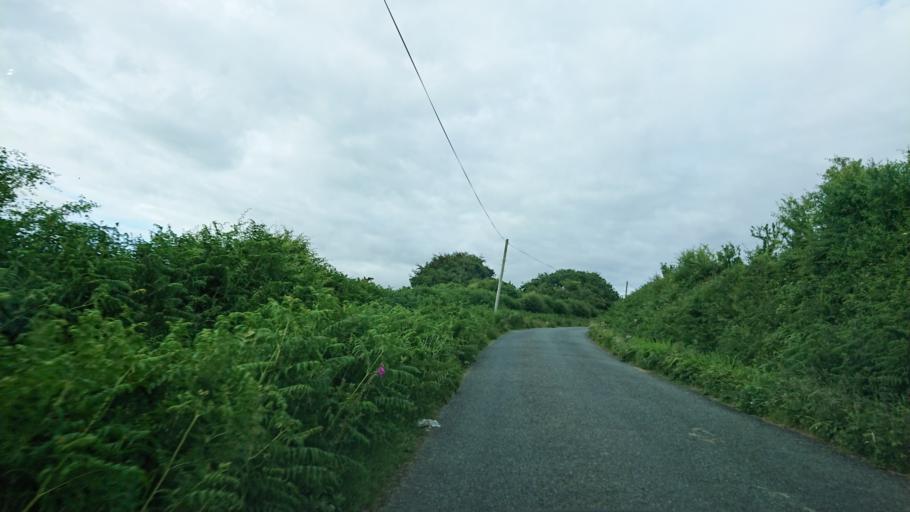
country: IE
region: Munster
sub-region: Waterford
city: Tra Mhor
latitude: 52.2051
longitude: -7.2182
